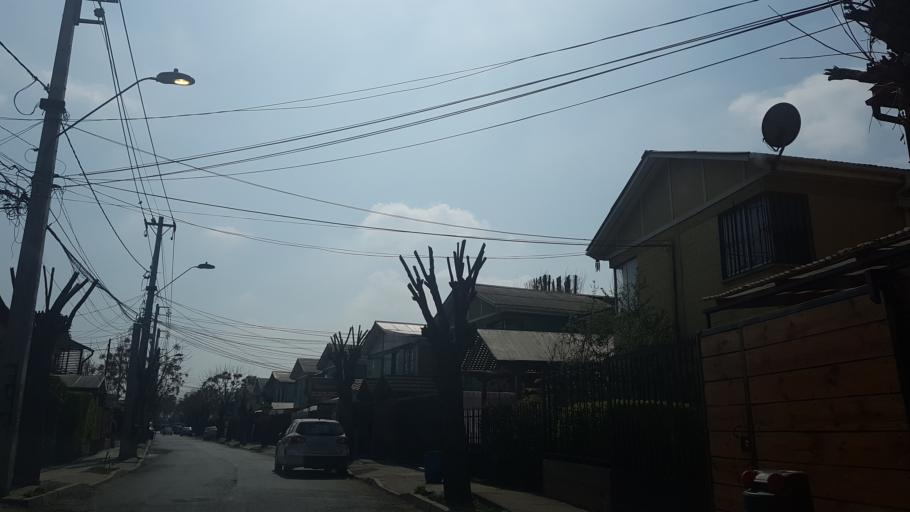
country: CL
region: Santiago Metropolitan
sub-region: Provincia de Santiago
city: Lo Prado
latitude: -33.3591
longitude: -70.7153
